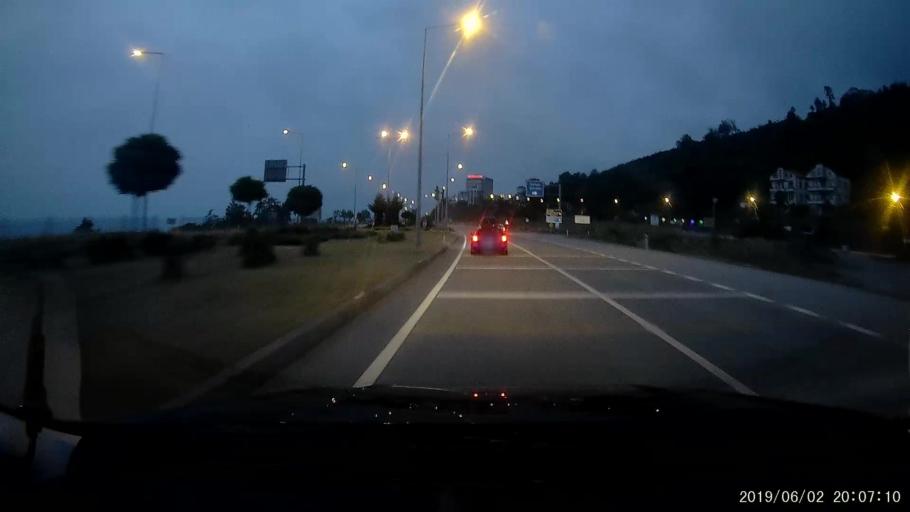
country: TR
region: Giresun
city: Gorele
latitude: 41.0364
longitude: 38.9711
